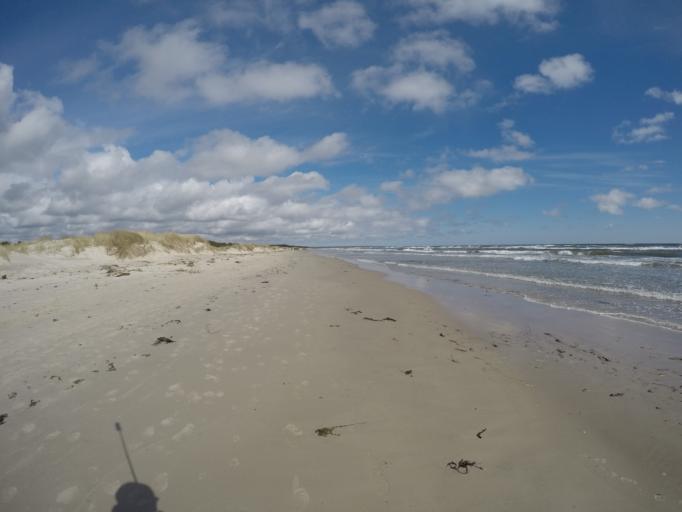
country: SE
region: Skane
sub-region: Simrishamns Kommun
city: Simrishamn
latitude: 55.4047
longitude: 14.2177
